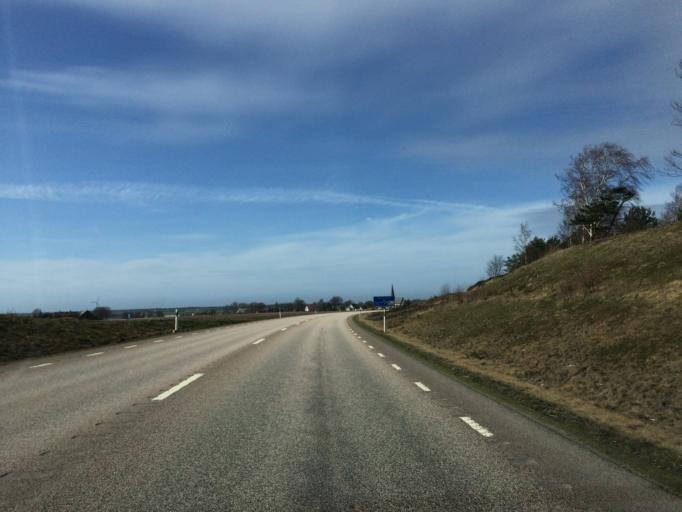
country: SE
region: Halland
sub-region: Laholms Kommun
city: Veinge
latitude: 56.5439
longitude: 13.0593
